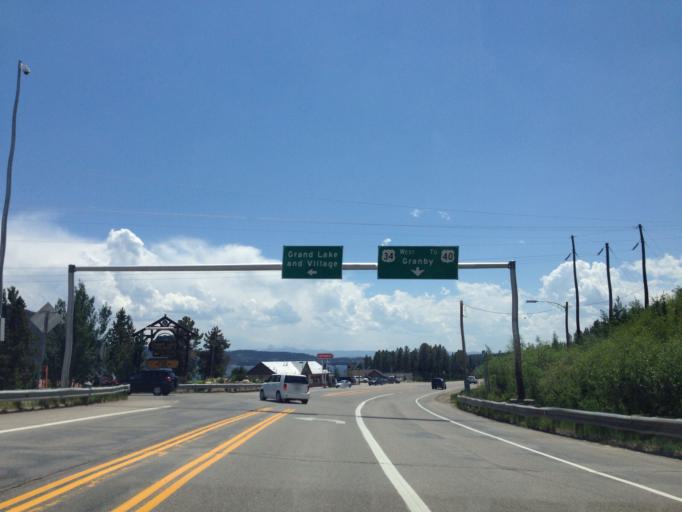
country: US
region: Colorado
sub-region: Grand County
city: Granby
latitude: 40.2517
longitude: -105.8351
